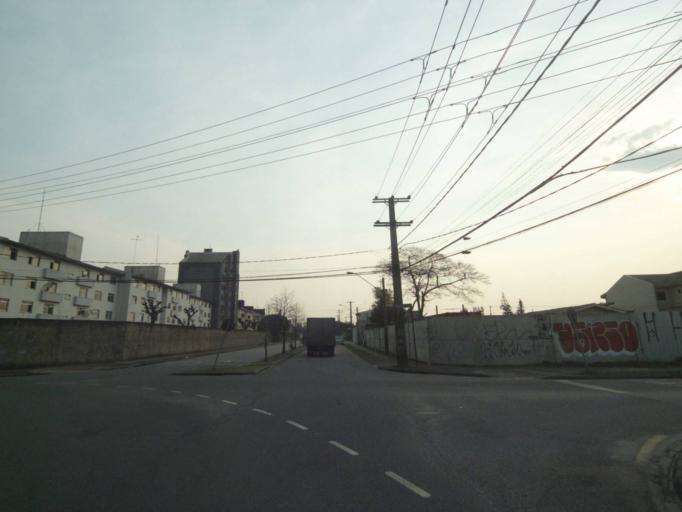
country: BR
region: Parana
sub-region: Curitiba
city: Curitiba
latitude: -25.4673
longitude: -49.2573
